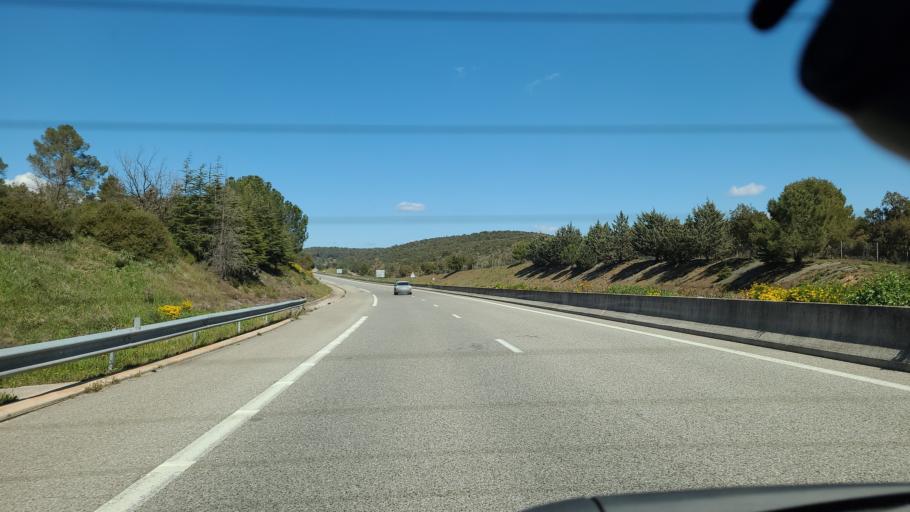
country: FR
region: Provence-Alpes-Cote d'Azur
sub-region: Departement du Var
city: Carnoules
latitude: 43.2756
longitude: 6.1864
